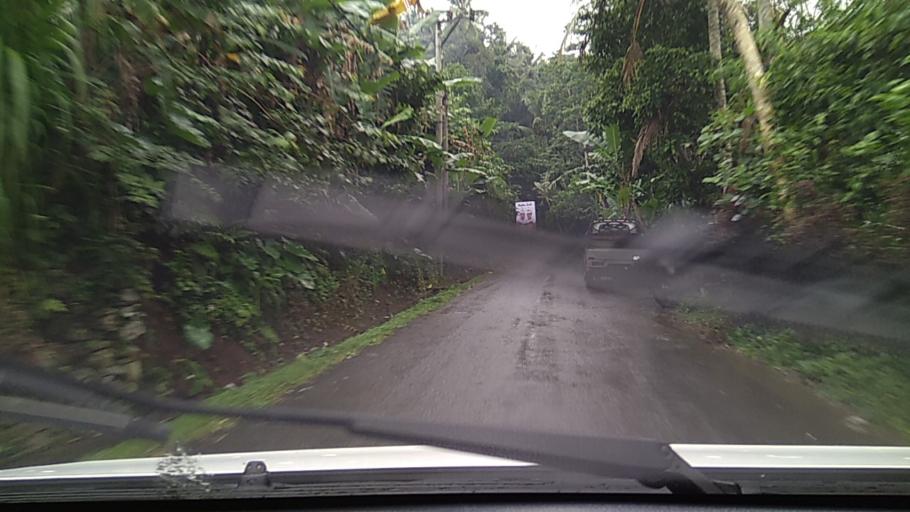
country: ID
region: Bali
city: Tiyingtali Kelod
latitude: -8.3934
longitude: 115.6211
